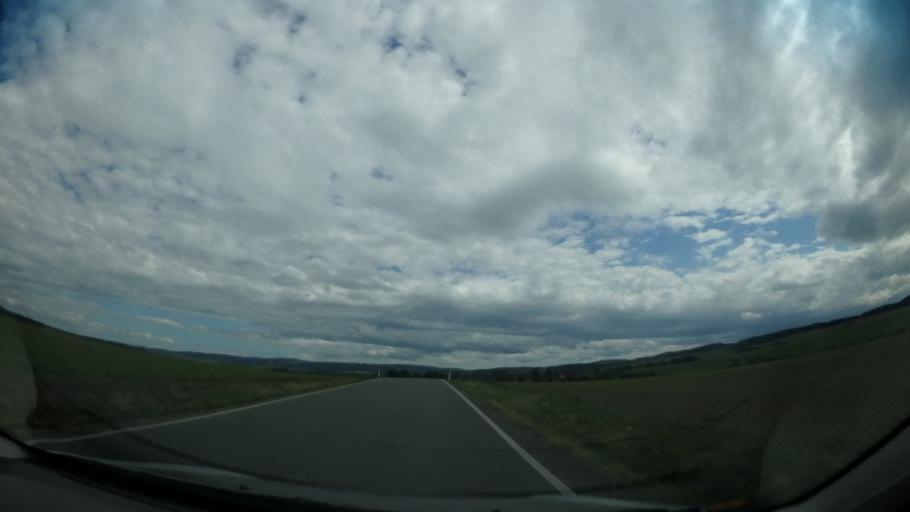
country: CZ
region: Pardubicky
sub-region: Okres Svitavy
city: Moravska Trebova
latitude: 49.8111
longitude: 16.6901
